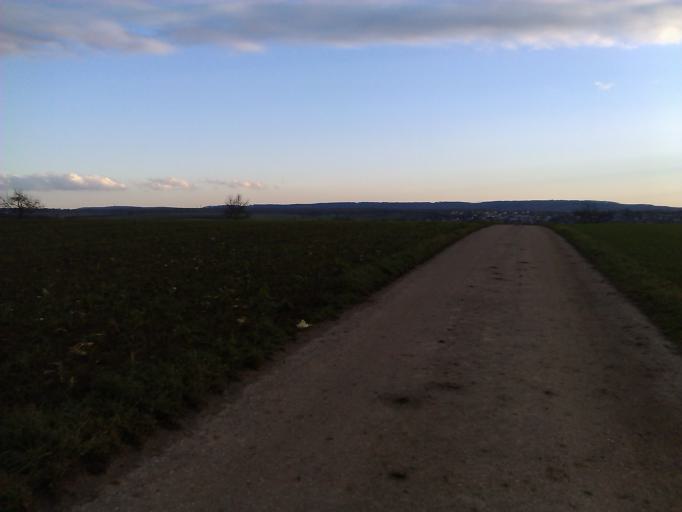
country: DE
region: Baden-Wuerttemberg
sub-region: Regierungsbezirk Stuttgart
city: Oedheim
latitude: 49.2550
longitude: 9.2534
